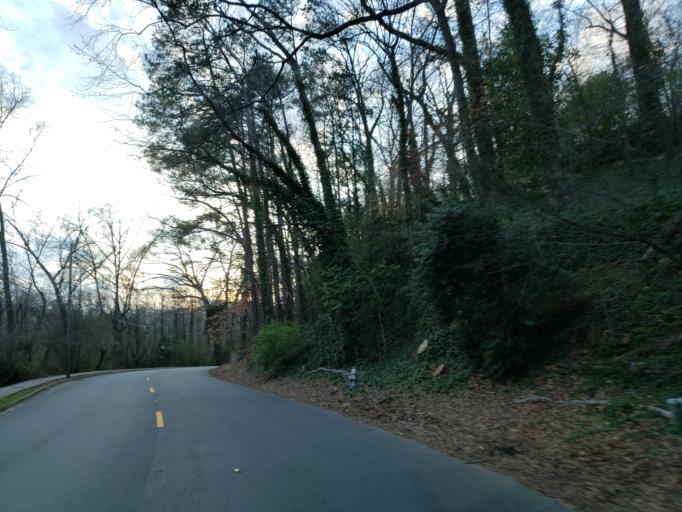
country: US
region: Georgia
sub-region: Cobb County
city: Vinings
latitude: 33.8247
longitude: -84.4130
